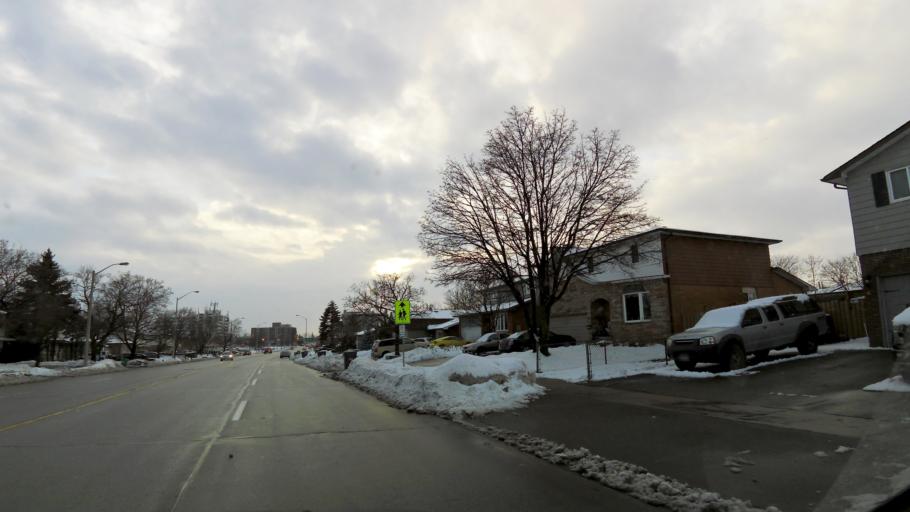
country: CA
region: Ontario
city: Brampton
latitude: 43.7056
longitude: -79.7559
